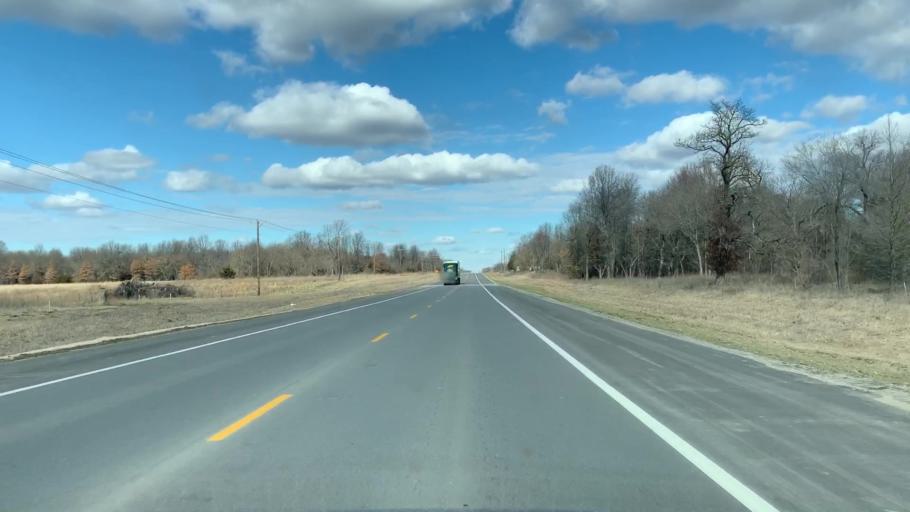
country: US
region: Kansas
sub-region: Cherokee County
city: Columbus
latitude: 37.2256
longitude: -94.8319
